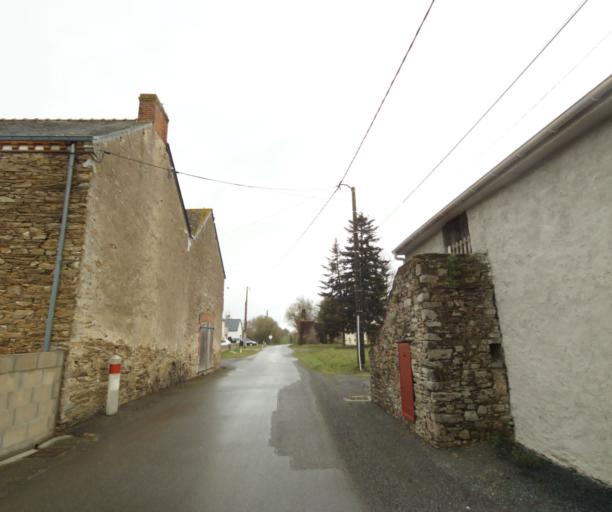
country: FR
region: Pays de la Loire
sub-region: Departement de la Loire-Atlantique
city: Bouvron
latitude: 47.4436
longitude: -1.8779
